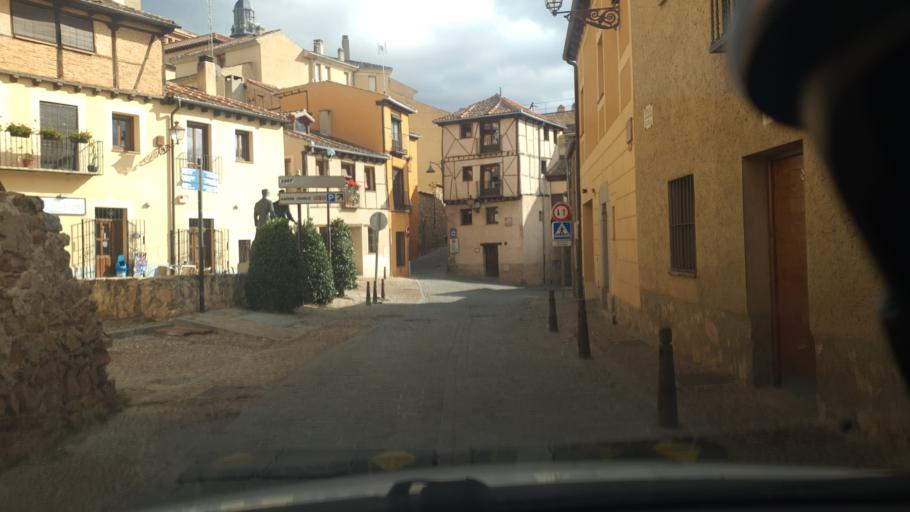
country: ES
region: Castille and Leon
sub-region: Provincia de Segovia
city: Segovia
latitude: 40.9502
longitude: -4.1276
